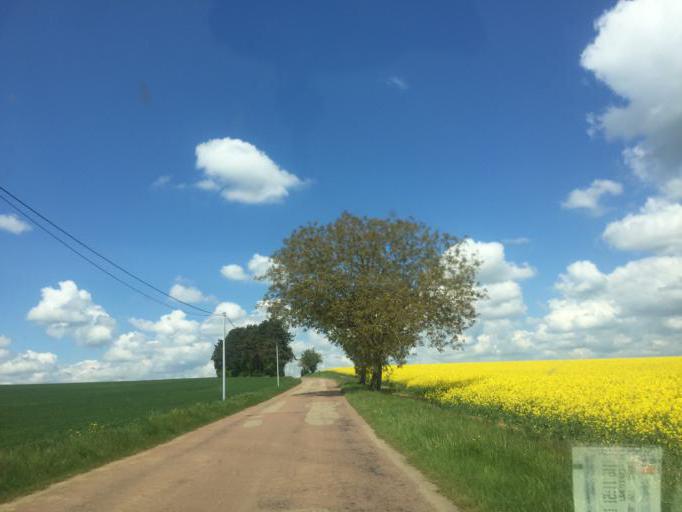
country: FR
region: Bourgogne
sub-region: Departement de l'Yonne
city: Fontenailles
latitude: 47.4990
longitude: 3.3641
